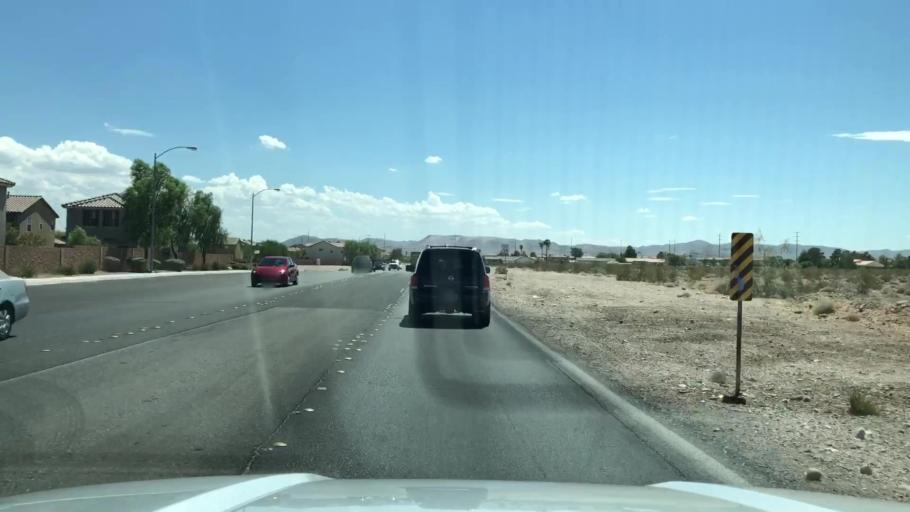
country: US
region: Nevada
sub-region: Clark County
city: Enterprise
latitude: 36.0418
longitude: -115.2079
